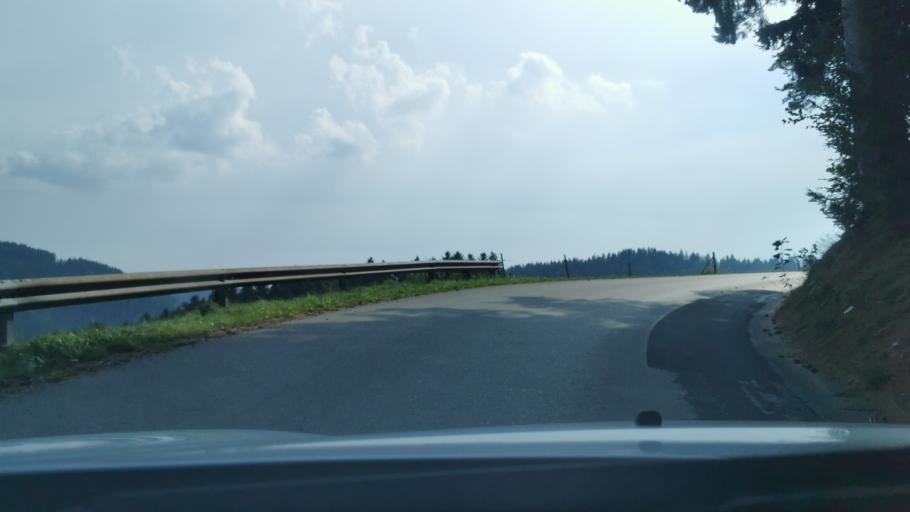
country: AT
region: Styria
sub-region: Politischer Bezirk Weiz
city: Strallegg
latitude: 47.3990
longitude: 15.6993
